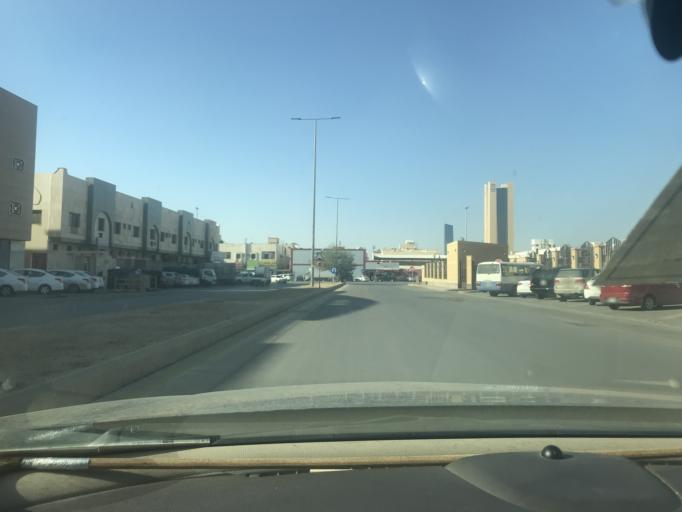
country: SA
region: Ar Riyad
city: Riyadh
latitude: 24.7524
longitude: 46.6663
